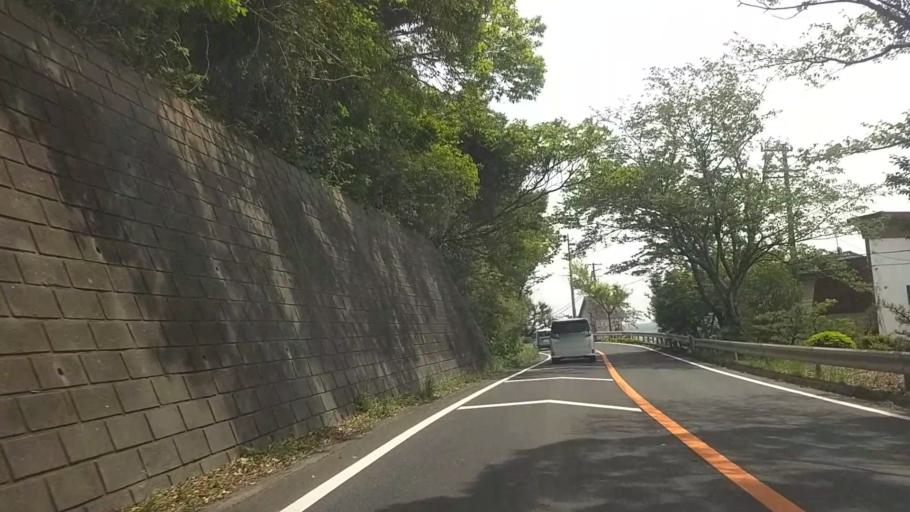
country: JP
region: Shizuoka
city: Kosai-shi
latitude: 34.7684
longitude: 137.5492
